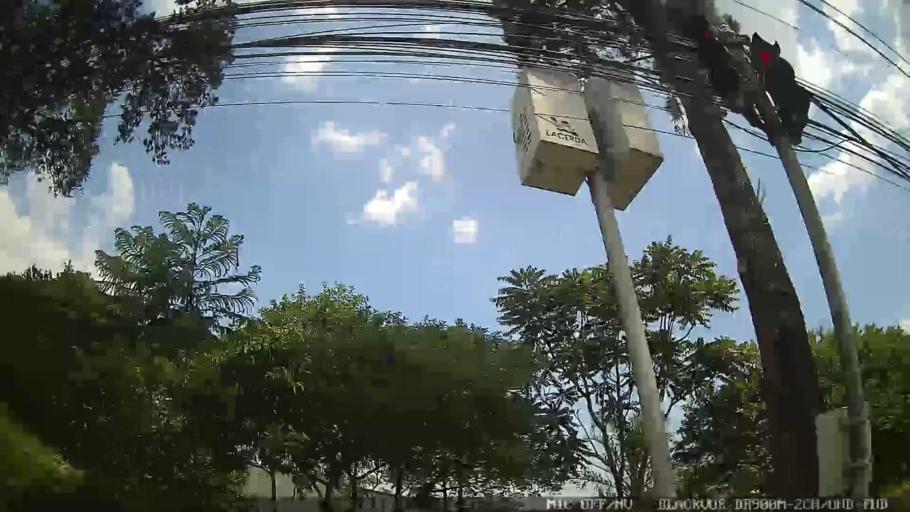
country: BR
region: Sao Paulo
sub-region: Taboao Da Serra
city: Taboao da Serra
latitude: -23.6633
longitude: -46.7814
